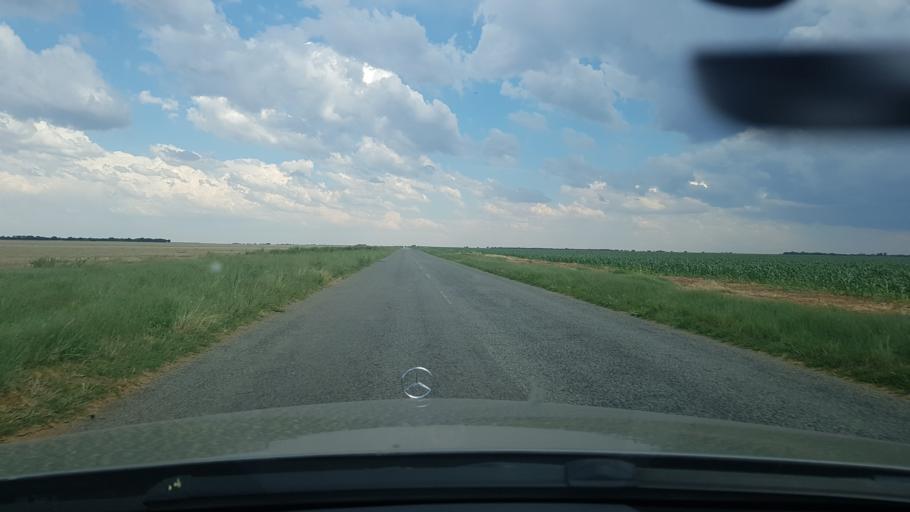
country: ZA
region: North-West
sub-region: Dr Ruth Segomotsi Mompati District Municipality
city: Bloemhof
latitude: -27.8796
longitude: 25.6632
